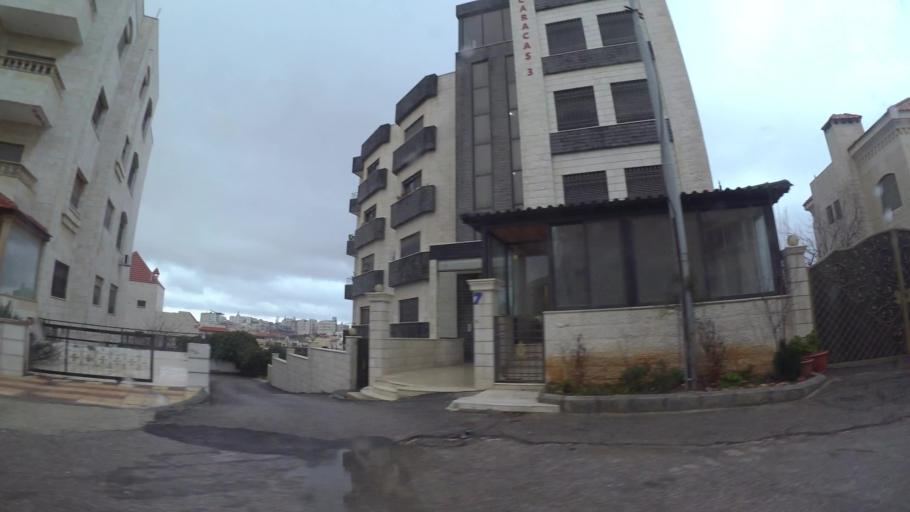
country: JO
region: Amman
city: Al Jubayhah
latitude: 32.0344
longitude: 35.8597
